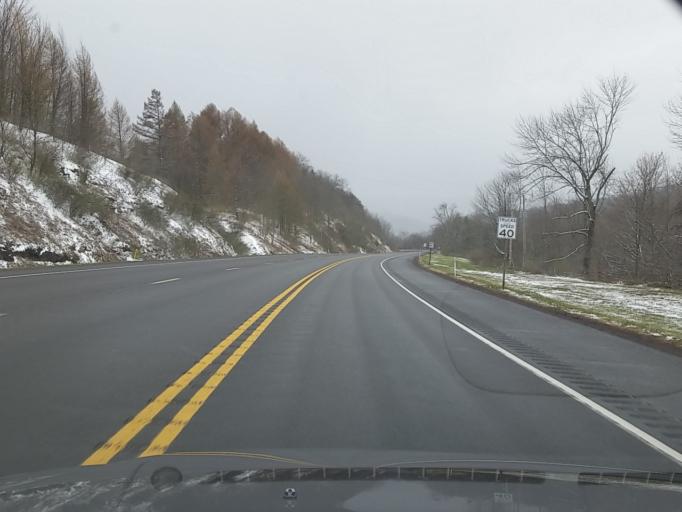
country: US
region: Pennsylvania
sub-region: Sullivan County
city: Laporte
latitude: 41.3676
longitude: -76.5301
